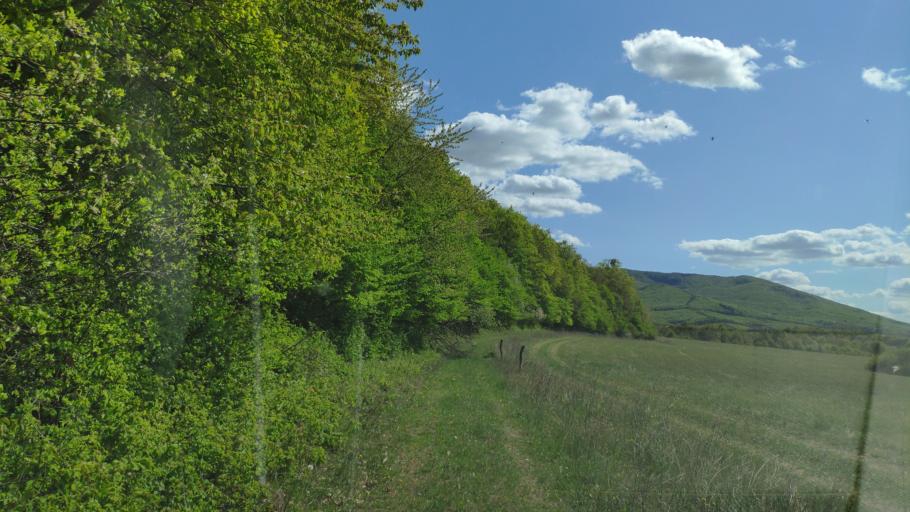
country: SK
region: Kosicky
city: Kosice
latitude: 48.6590
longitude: 21.4303
